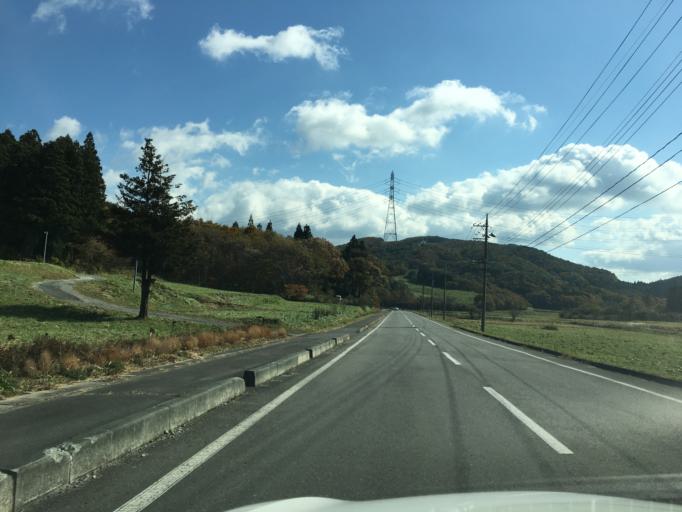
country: JP
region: Fukushima
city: Funehikimachi-funehiki
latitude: 37.2943
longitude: 140.7141
